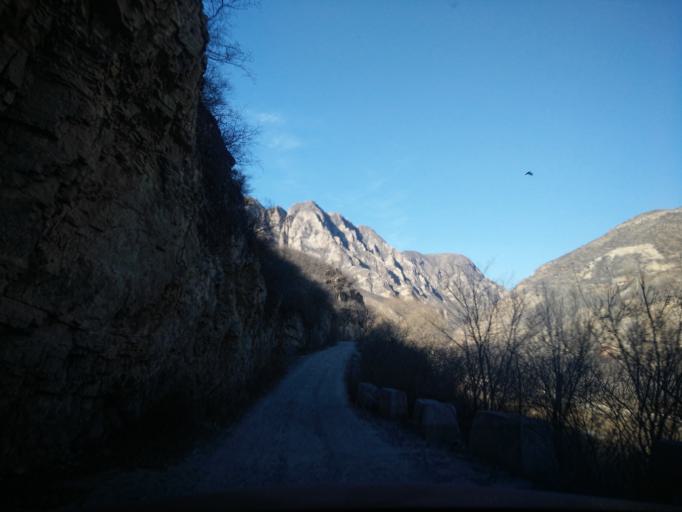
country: CN
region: Beijing
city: Yanjiatai
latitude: 40.1651
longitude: 115.6490
